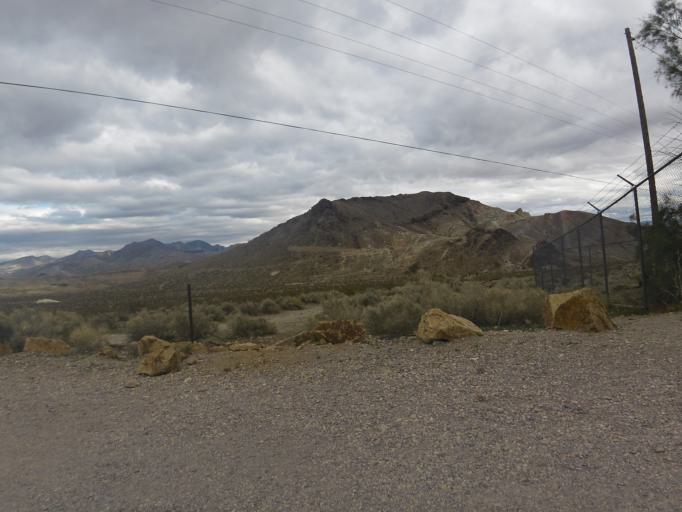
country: US
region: Nevada
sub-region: Nye County
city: Beatty
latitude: 36.9036
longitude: -116.8285
